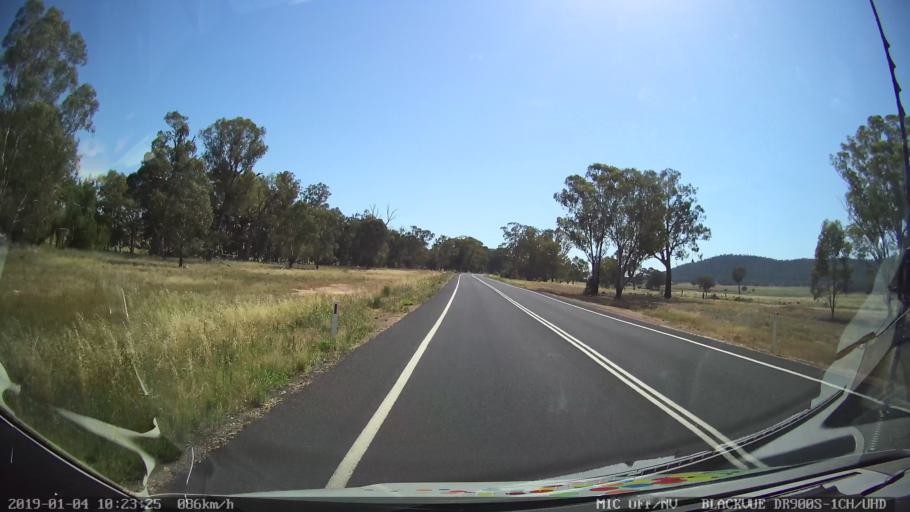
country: AU
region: New South Wales
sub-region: Cabonne
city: Canowindra
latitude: -33.3715
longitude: 148.5392
